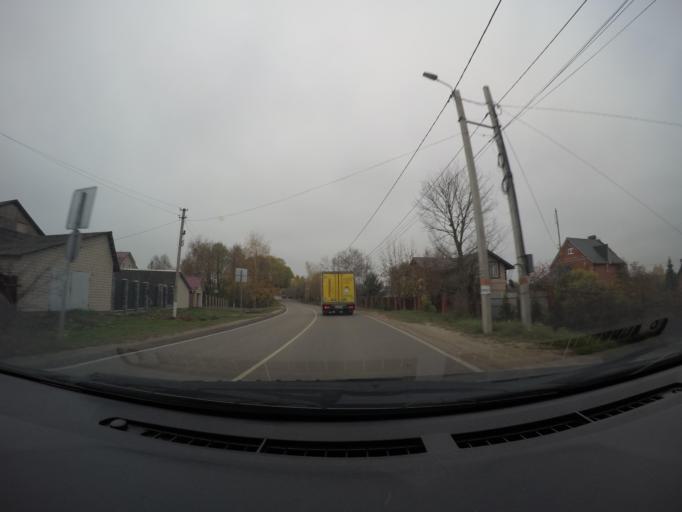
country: RU
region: Moskovskaya
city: Gzhel'
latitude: 55.5790
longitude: 38.3967
